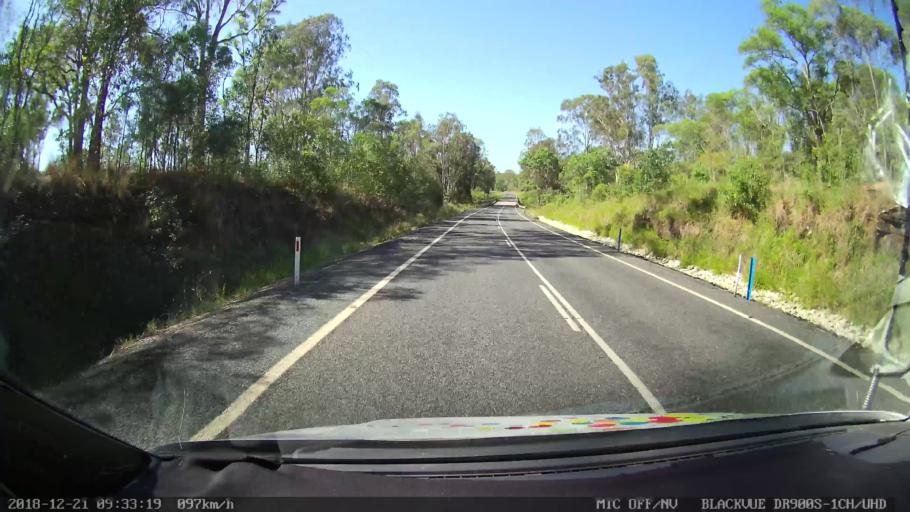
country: AU
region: New South Wales
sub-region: Clarence Valley
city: Grafton
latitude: -29.4827
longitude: 152.9768
